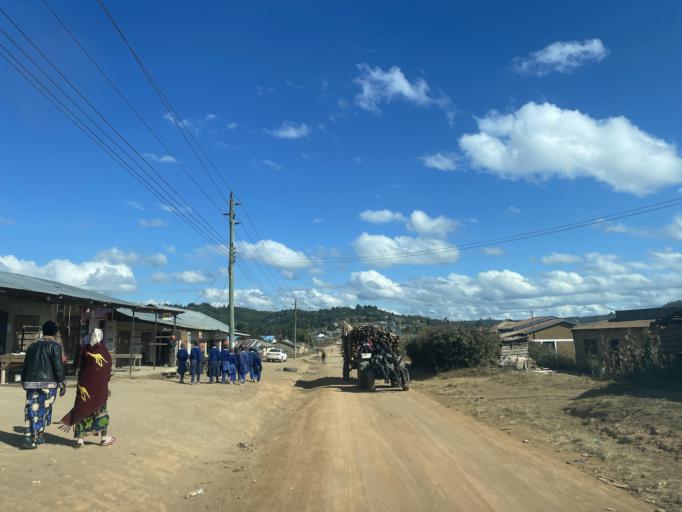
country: TZ
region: Iringa
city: Makungu
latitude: -8.4194
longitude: 35.4200
